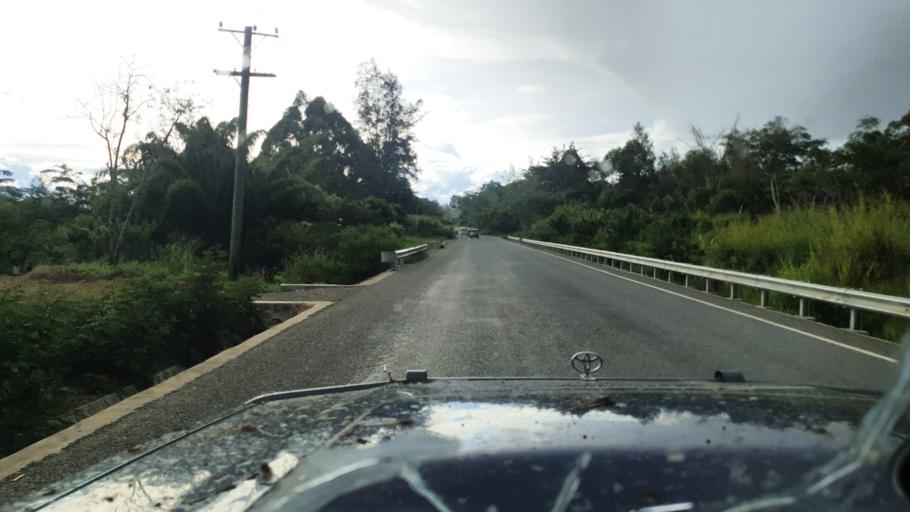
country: PG
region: Jiwaka
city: Minj
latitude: -5.9345
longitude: 144.8037
